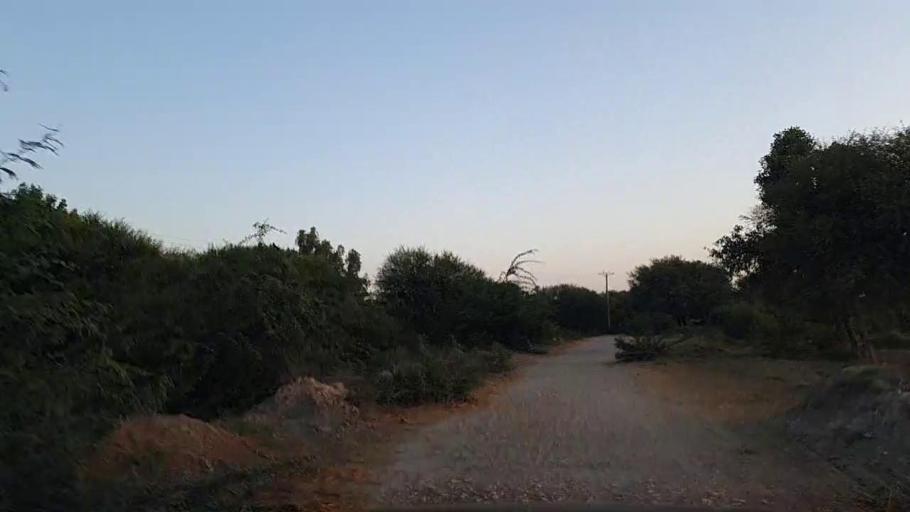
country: PK
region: Sindh
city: Mirpur Batoro
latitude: 24.6364
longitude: 68.1906
